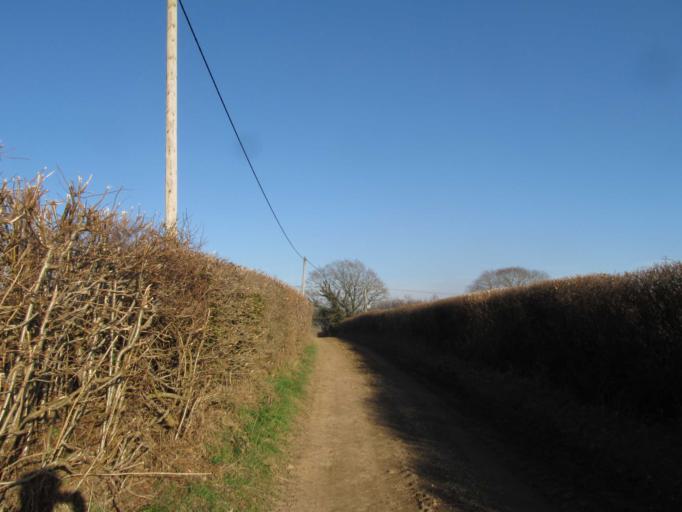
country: GB
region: England
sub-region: West Sussex
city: Petworth
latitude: 50.9787
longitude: -0.6266
